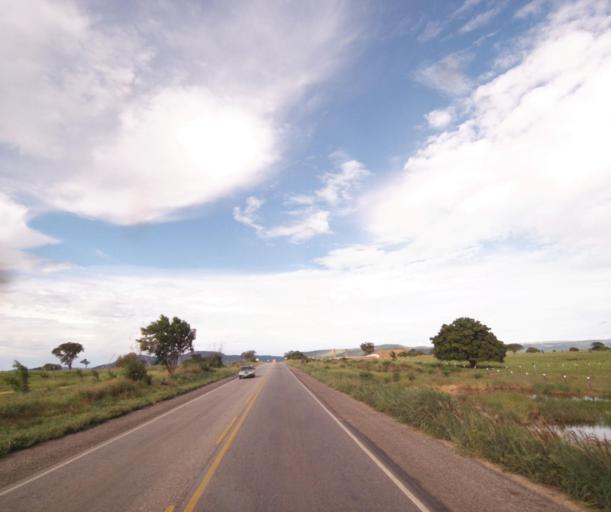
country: BR
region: Bahia
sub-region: Guanambi
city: Guanambi
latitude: -14.1946
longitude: -42.7481
